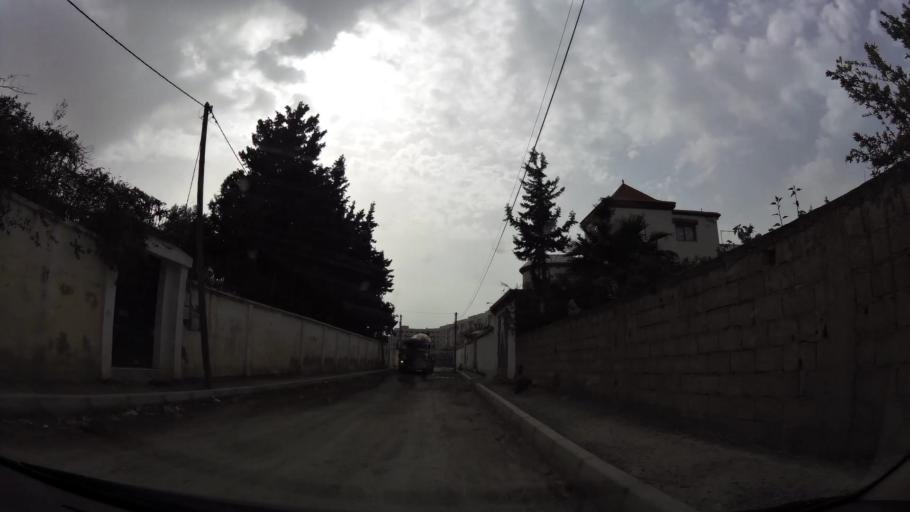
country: MA
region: Tanger-Tetouan
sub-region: Tanger-Assilah
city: Boukhalef
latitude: 35.7073
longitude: -5.9005
